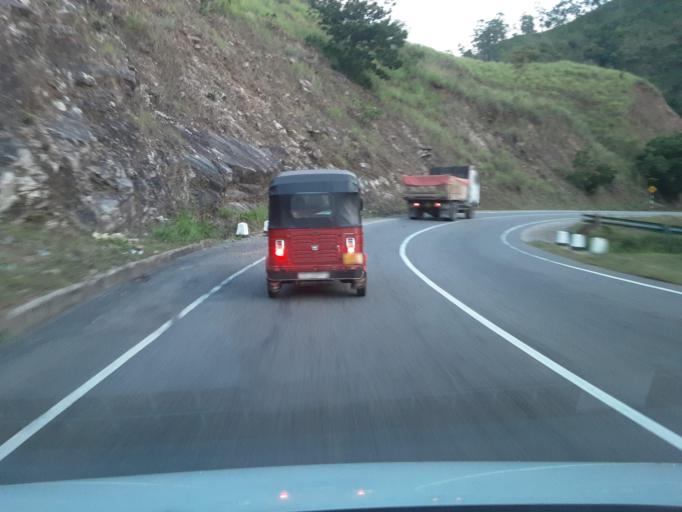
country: LK
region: Uva
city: Badulla
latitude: 6.9151
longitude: 80.9552
